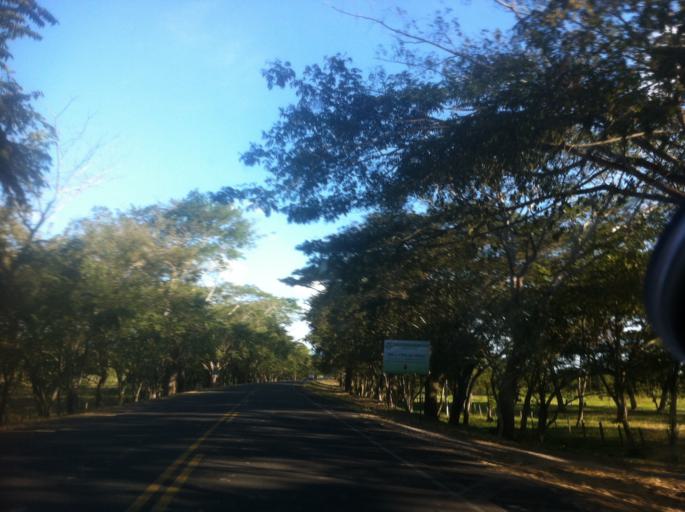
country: NI
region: Rio San Juan
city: Morrito
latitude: 11.7051
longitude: -84.9492
